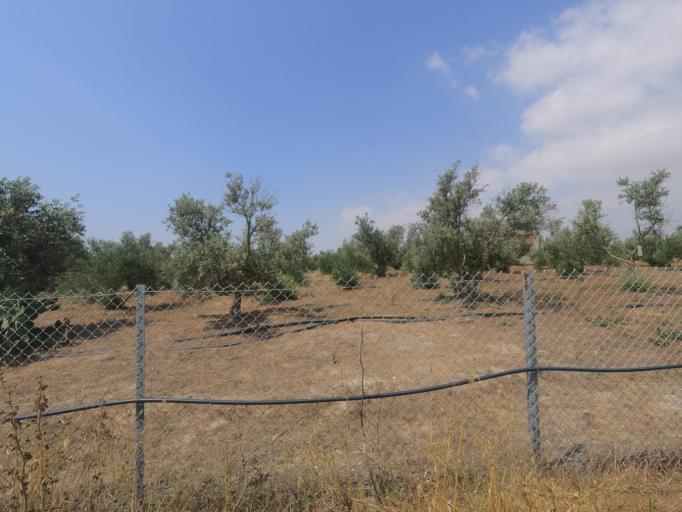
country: CY
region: Larnaka
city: Aradippou
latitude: 34.9629
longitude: 33.6069
